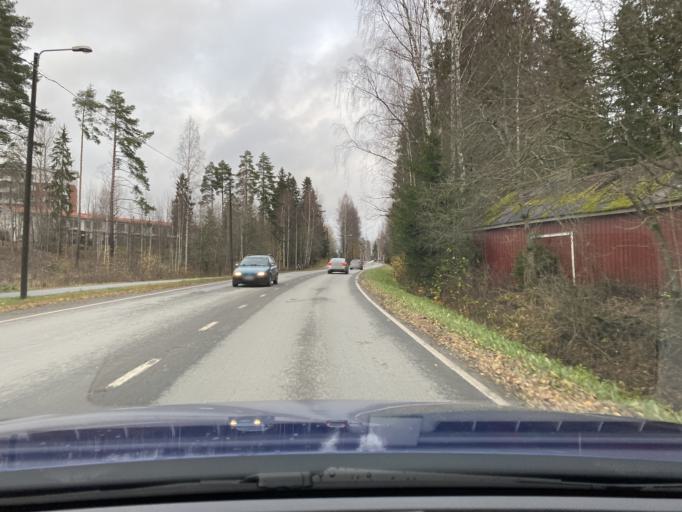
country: FI
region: Pirkanmaa
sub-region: Tampere
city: Lempaeaelae
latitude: 61.3350
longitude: 23.7504
